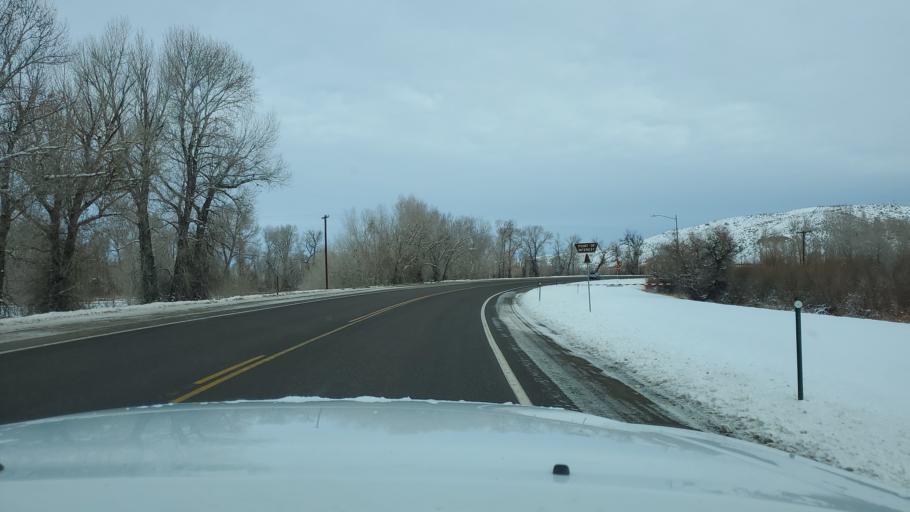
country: US
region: Colorado
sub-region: Routt County
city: Hayden
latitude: 40.5012
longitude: -107.3773
